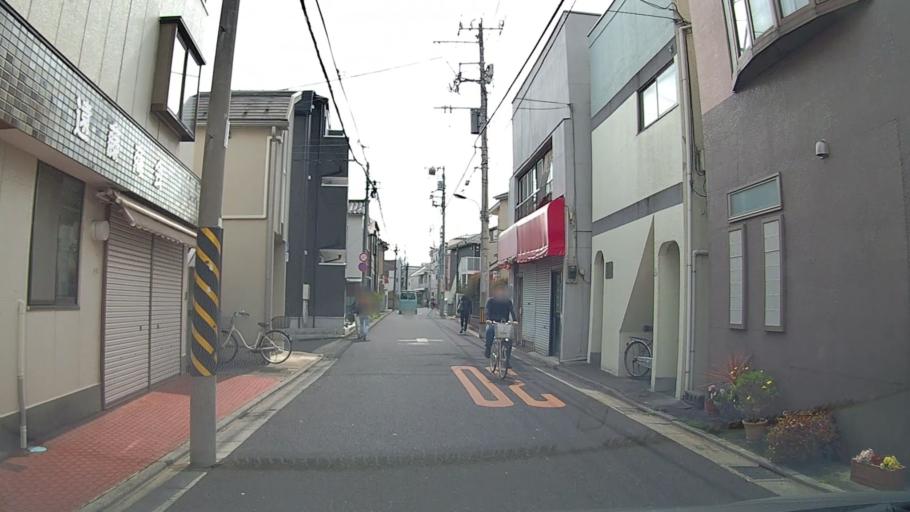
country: JP
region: Saitama
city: Wako
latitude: 35.7464
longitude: 139.6557
